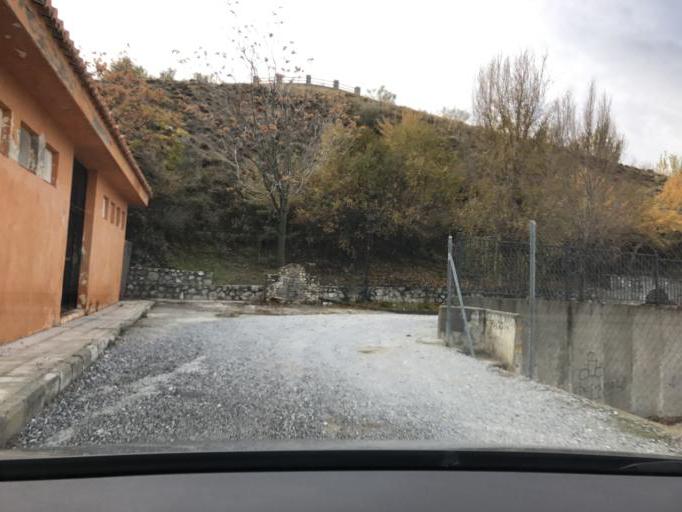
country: ES
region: Andalusia
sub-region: Provincia de Granada
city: Beas de Granada
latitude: 37.2160
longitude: -3.4790
